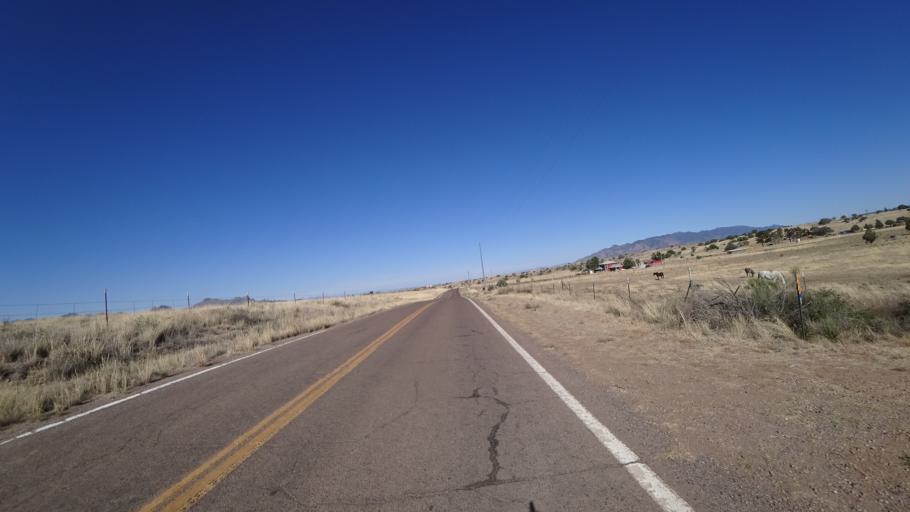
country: US
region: Arizona
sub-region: Cochise County
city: Huachuca City
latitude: 31.6080
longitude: -110.5848
